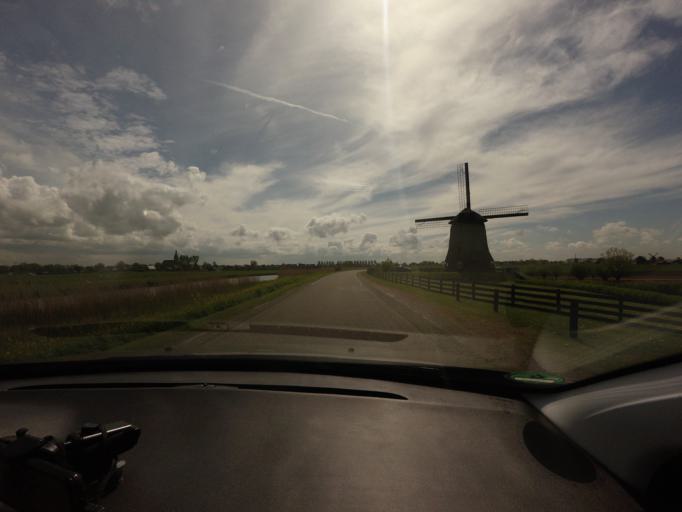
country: NL
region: North Holland
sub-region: Gemeente Heerhugowaard
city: Heerhugowaard
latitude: 52.6061
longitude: 4.8838
